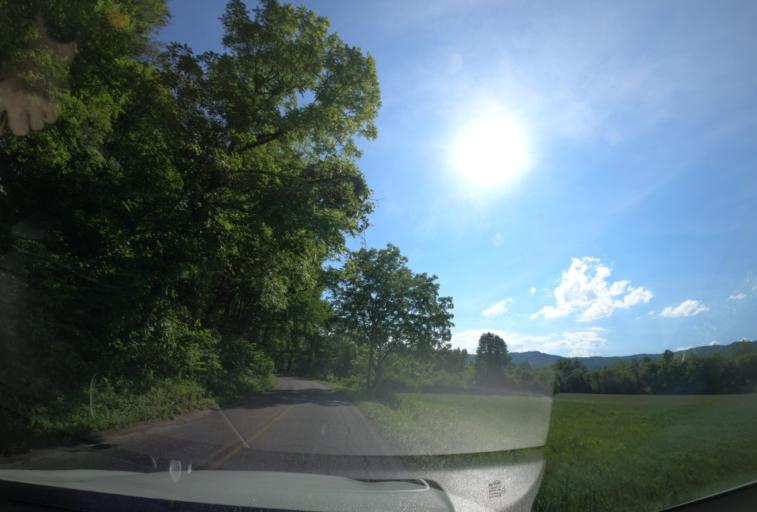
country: US
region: North Carolina
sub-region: Henderson County
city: Etowah
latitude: 35.2336
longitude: -82.6372
